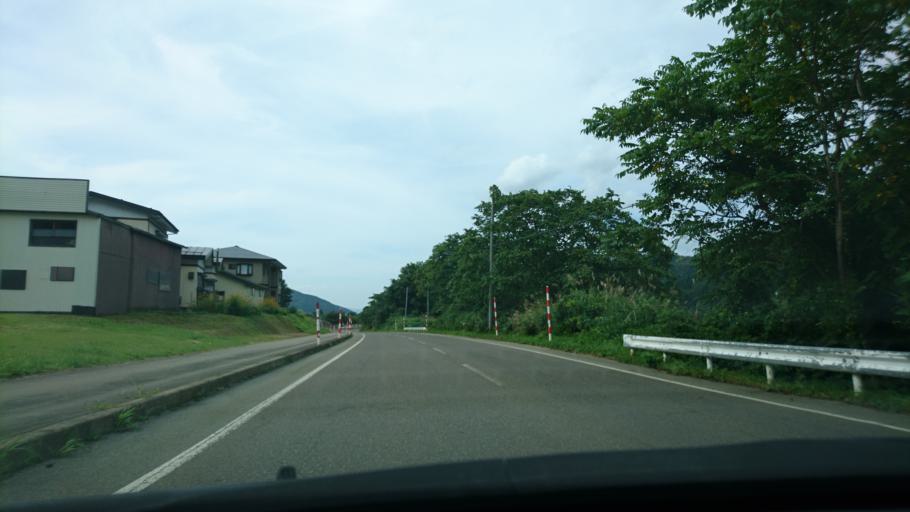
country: JP
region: Akita
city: Yuzawa
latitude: 39.1797
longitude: 140.6546
